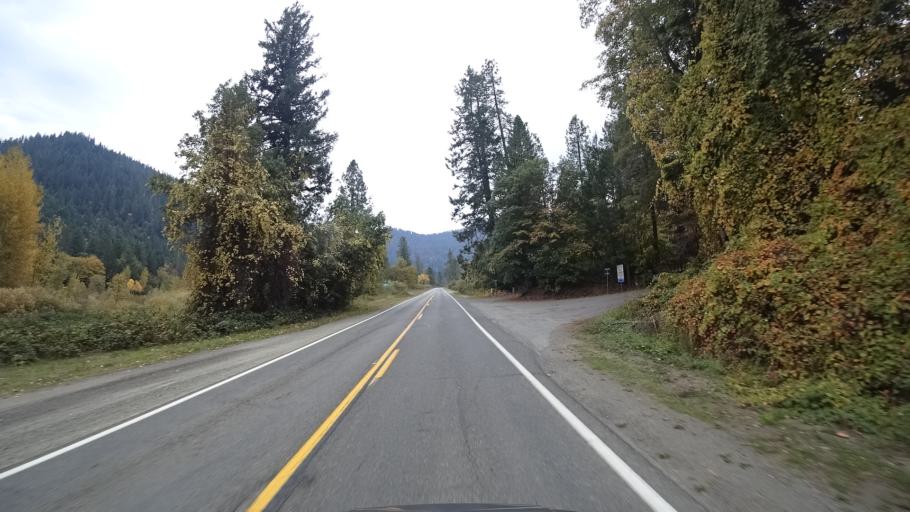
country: US
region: California
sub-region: Siskiyou County
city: Happy Camp
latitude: 41.7799
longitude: -123.3961
